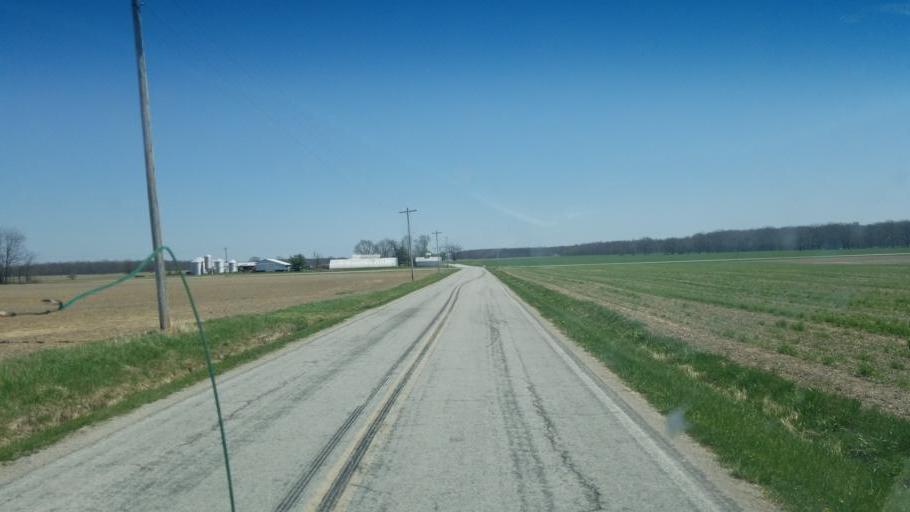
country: US
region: Ohio
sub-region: Huron County
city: New London
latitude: 41.1019
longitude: -82.3510
